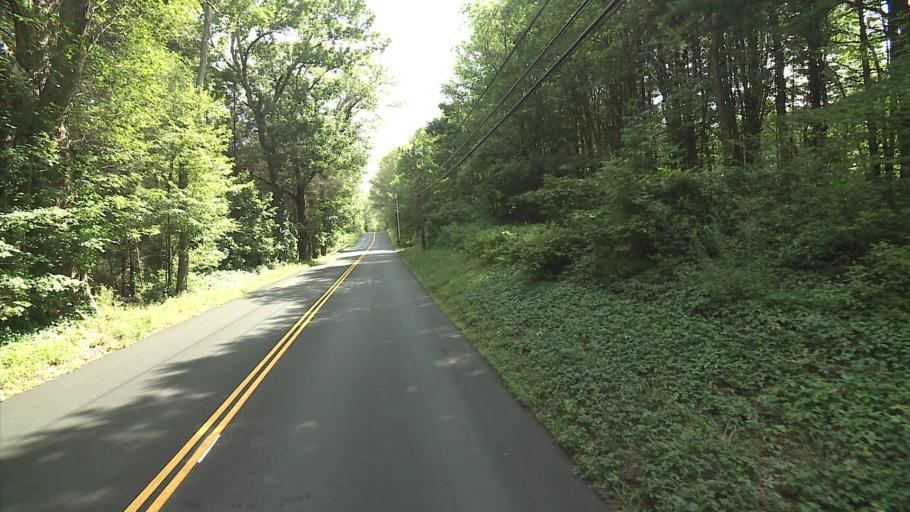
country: US
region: Connecticut
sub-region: Windham County
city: South Woodstock
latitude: 41.9444
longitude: -72.0668
